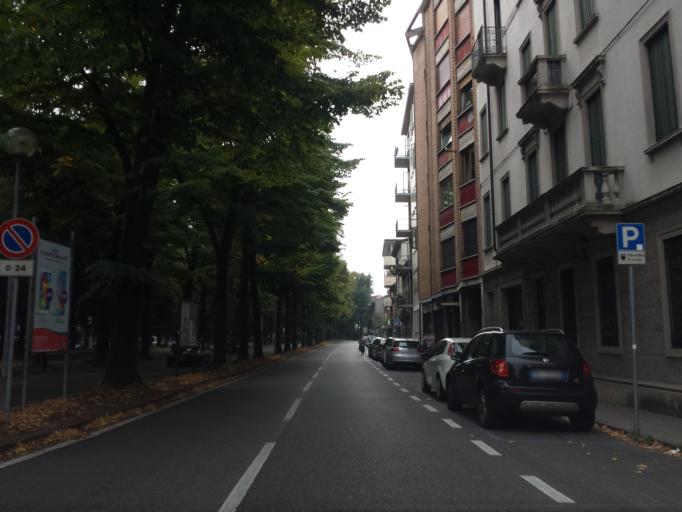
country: IT
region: Veneto
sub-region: Provincia di Padova
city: Padova
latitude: 45.4100
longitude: 11.8829
